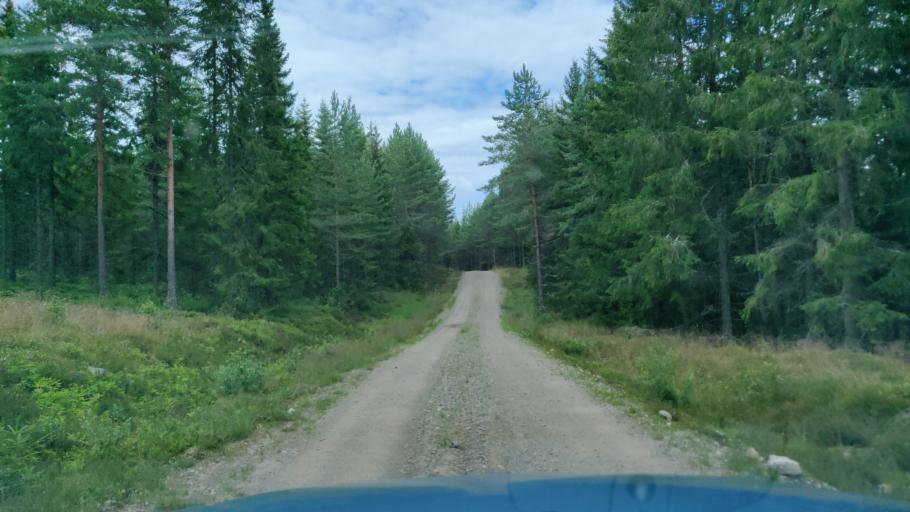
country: SE
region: Vaermland
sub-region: Hagfors Kommun
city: Hagfors
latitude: 59.9586
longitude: 13.5894
